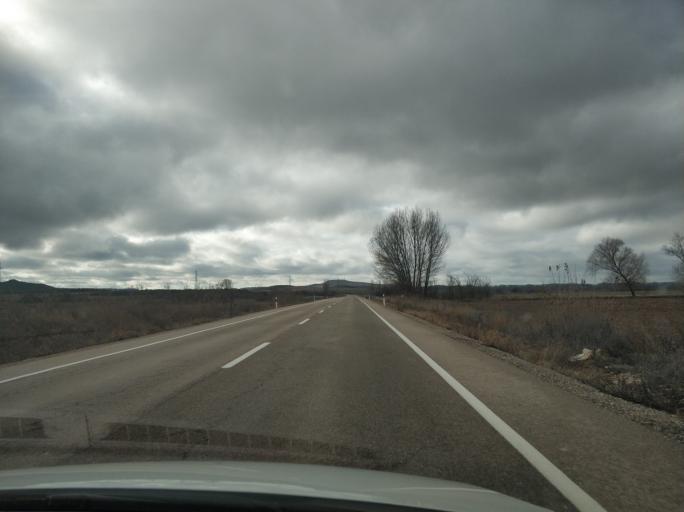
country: ES
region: Castille and Leon
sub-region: Provincia de Soria
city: San Esteban de Gormaz
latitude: 41.5675
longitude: -3.2303
